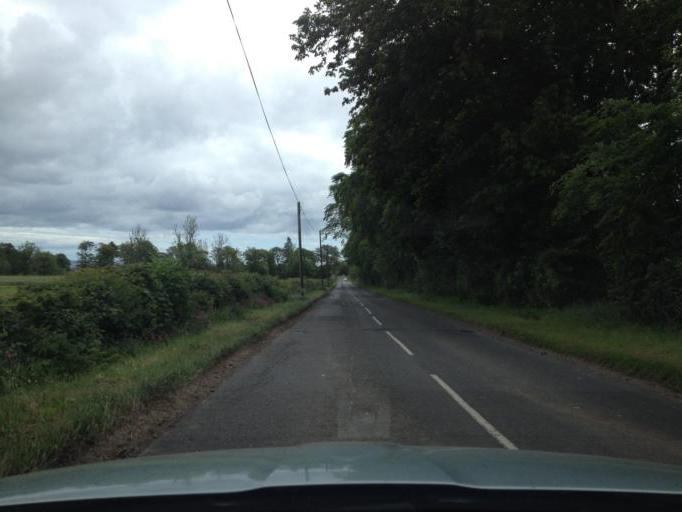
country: GB
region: Scotland
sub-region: Fife
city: Strathkinness
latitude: 56.3213
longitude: -2.8600
